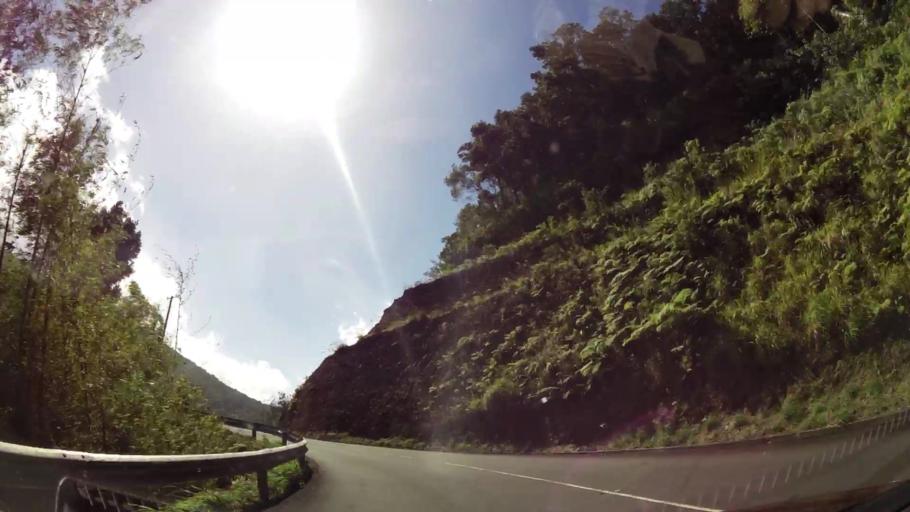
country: DM
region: Saint Paul
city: Pont Casse
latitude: 15.3561
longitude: -61.3575
